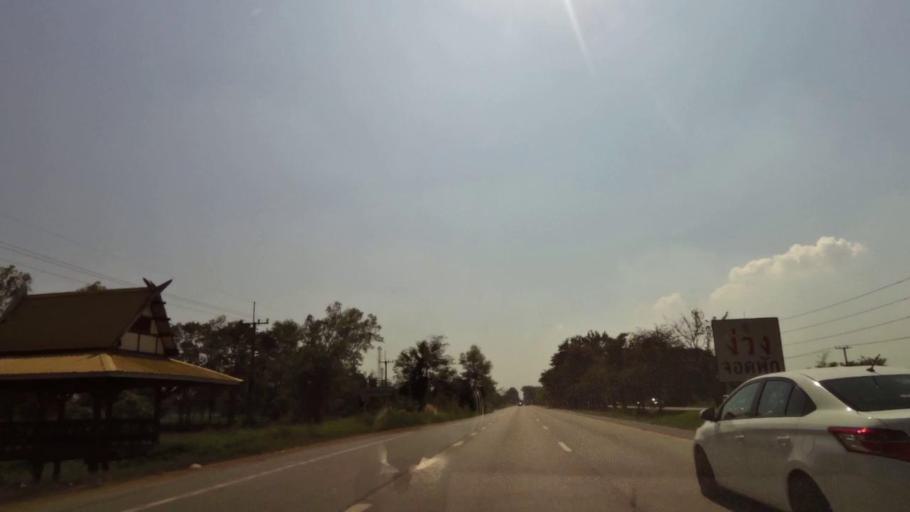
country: TH
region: Phichit
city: Wachira Barami
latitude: 16.5851
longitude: 100.1471
